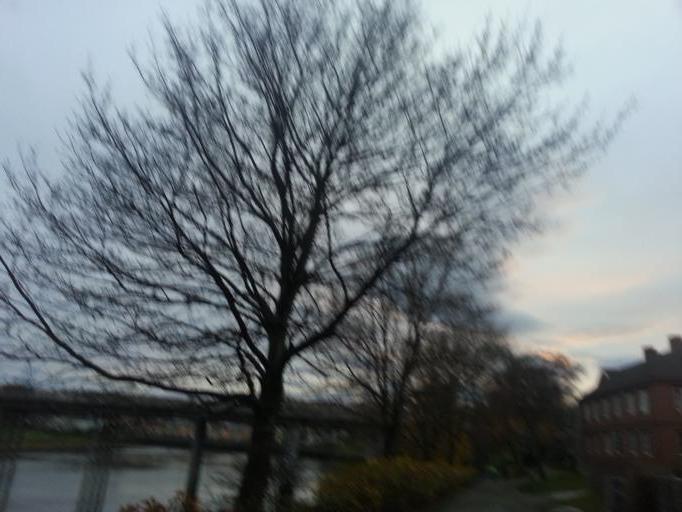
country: NO
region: Sor-Trondelag
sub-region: Trondheim
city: Trondheim
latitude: 63.4235
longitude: 10.3914
